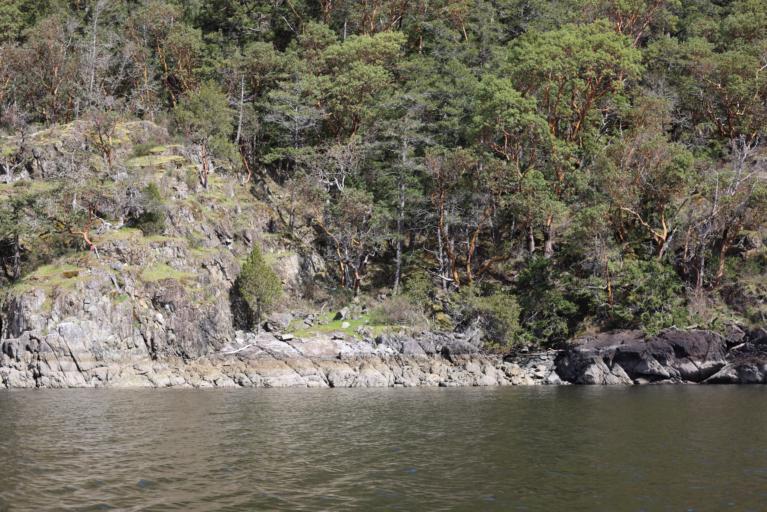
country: CA
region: British Columbia
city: Langford
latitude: 48.5606
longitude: -123.5243
